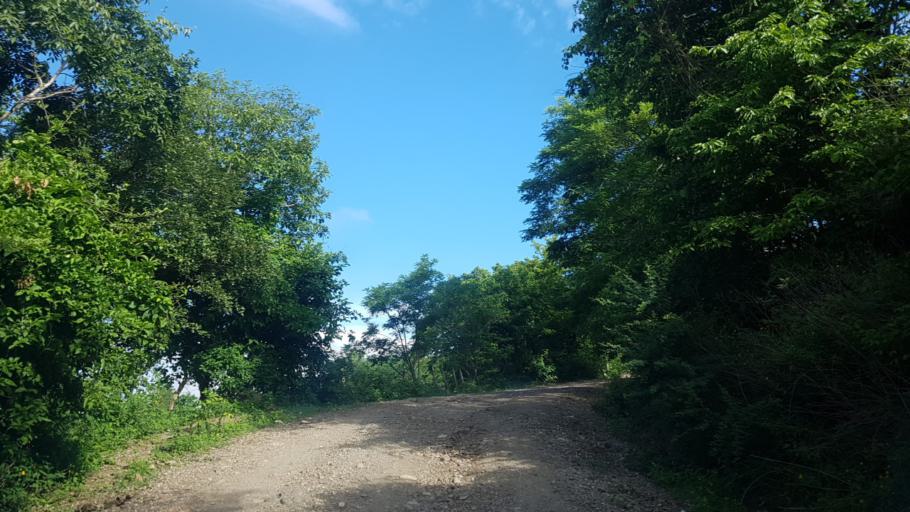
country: NI
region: Nueva Segovia
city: Ocotal
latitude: 13.6073
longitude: -86.4607
